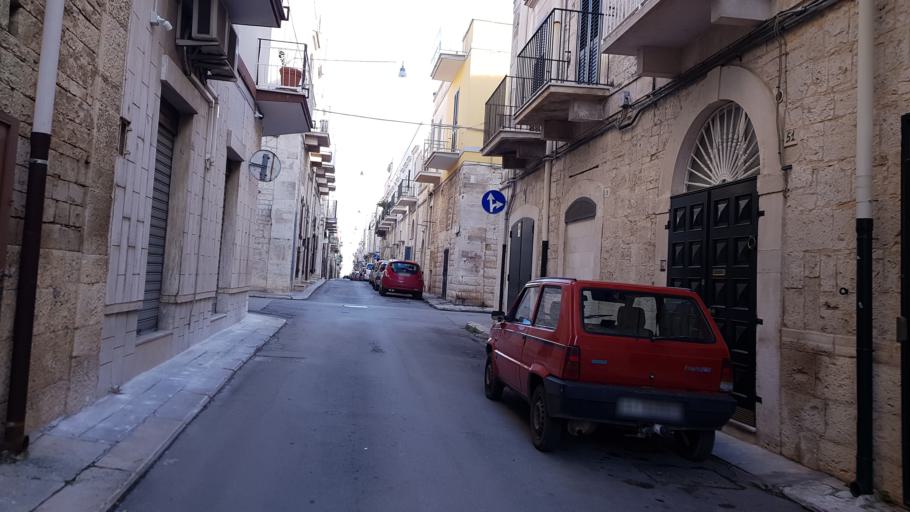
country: IT
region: Apulia
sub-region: Provincia di Bari
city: Ruvo di Puglia
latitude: 41.1195
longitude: 16.4847
